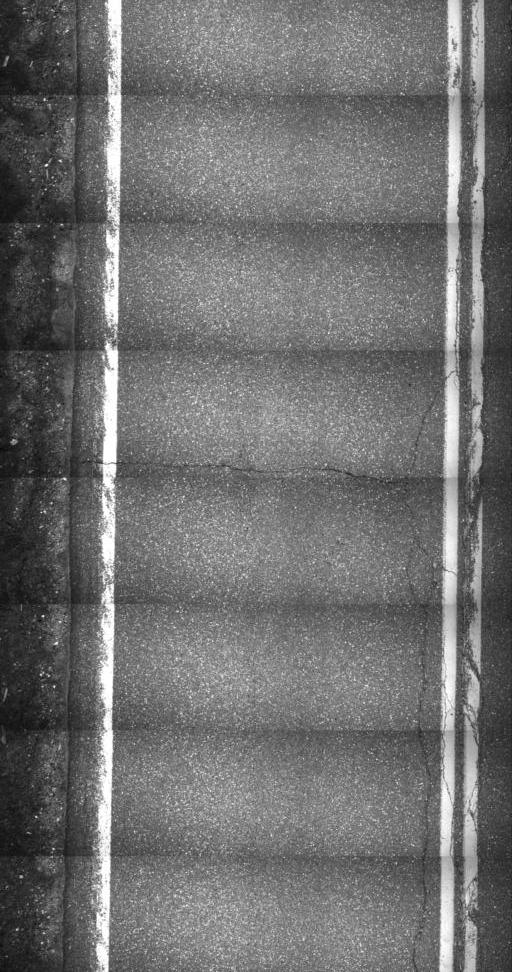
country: US
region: New Hampshire
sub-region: Grafton County
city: Woodsville
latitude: 44.2413
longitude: -72.2407
